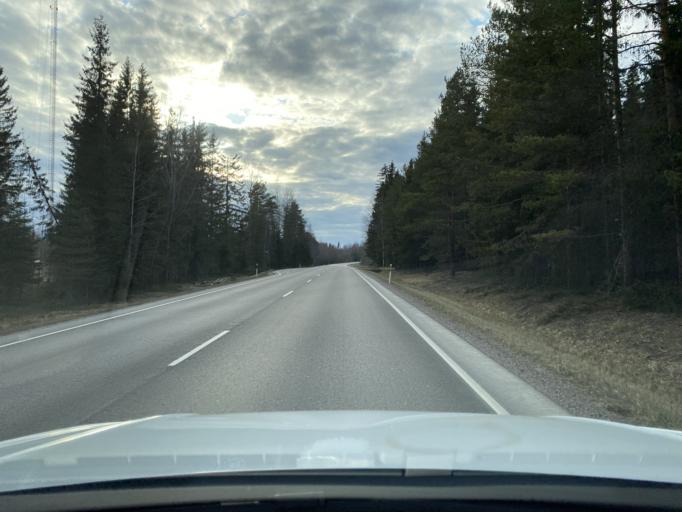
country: FI
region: Haeme
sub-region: Haemeenlinna
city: Renko
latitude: 60.7862
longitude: 24.1407
